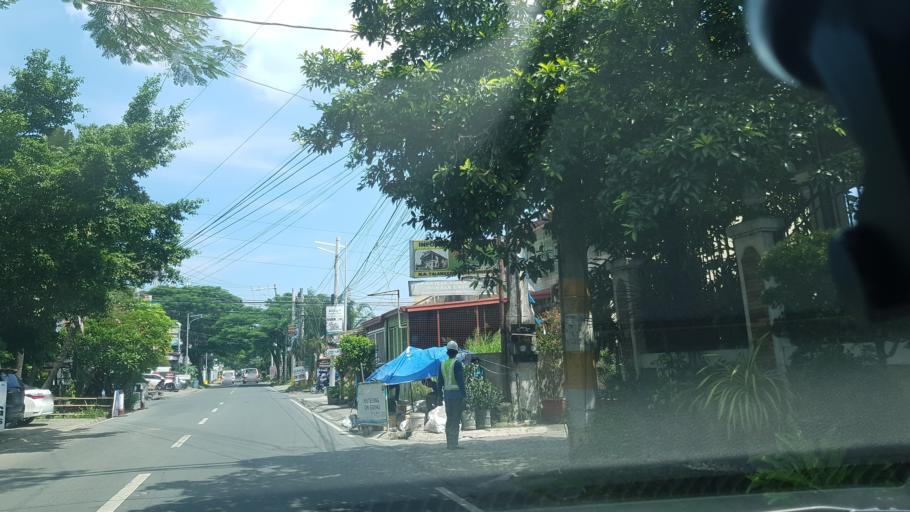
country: PH
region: Calabarzon
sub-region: Province of Rizal
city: Las Pinas
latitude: 14.4297
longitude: 120.9944
